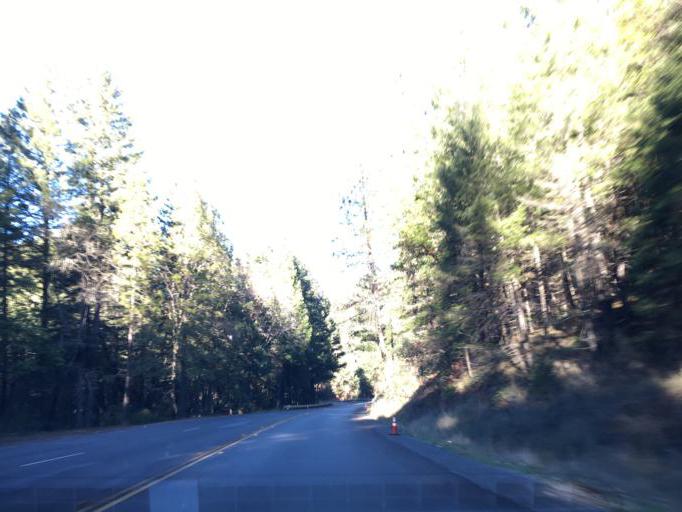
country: US
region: California
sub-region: Mendocino County
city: Laytonville
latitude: 39.7894
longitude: -123.5436
